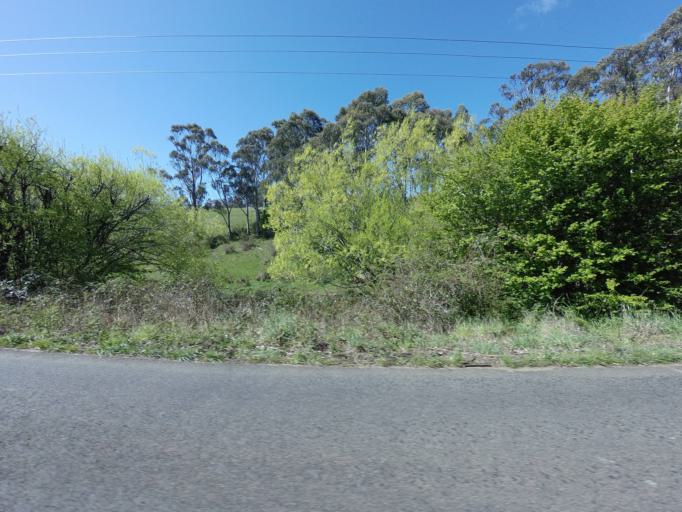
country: AU
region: Tasmania
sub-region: Derwent Valley
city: New Norfolk
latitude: -42.6253
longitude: 146.7228
